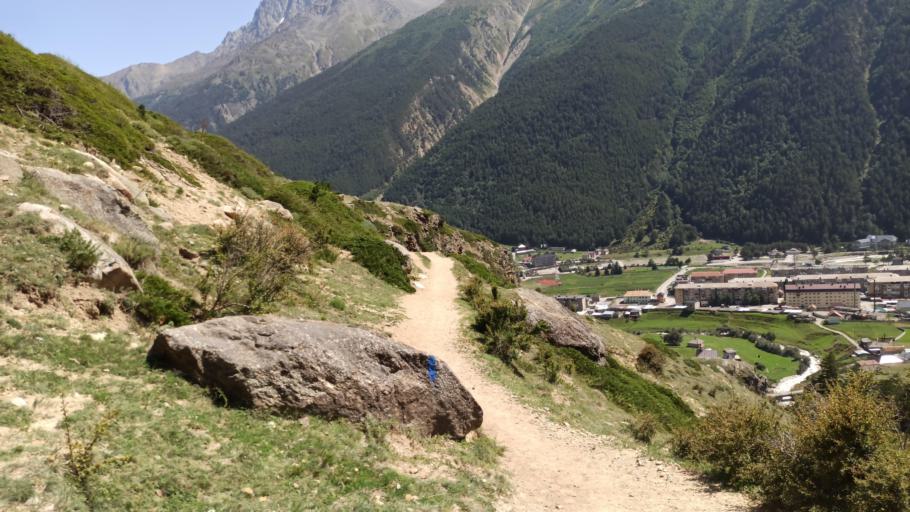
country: RU
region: Kabardino-Balkariya
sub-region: El'brusskiy Rayon
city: El'brus
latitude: 43.2628
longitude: 42.6386
